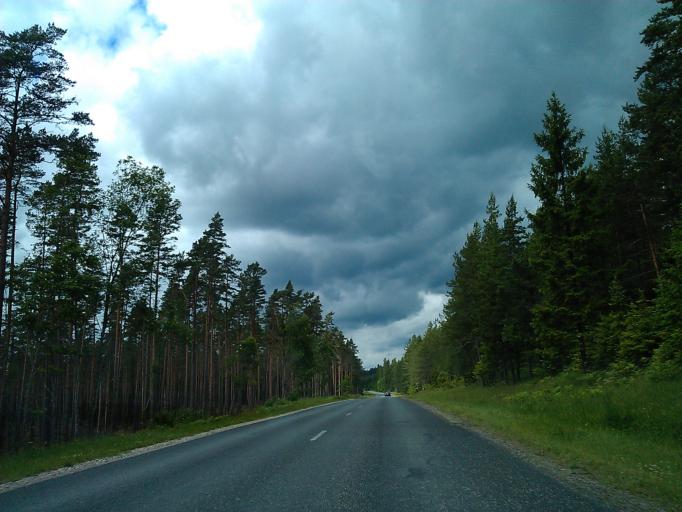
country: LV
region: Talsu Rajons
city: Stende
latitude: 57.0845
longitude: 22.4250
